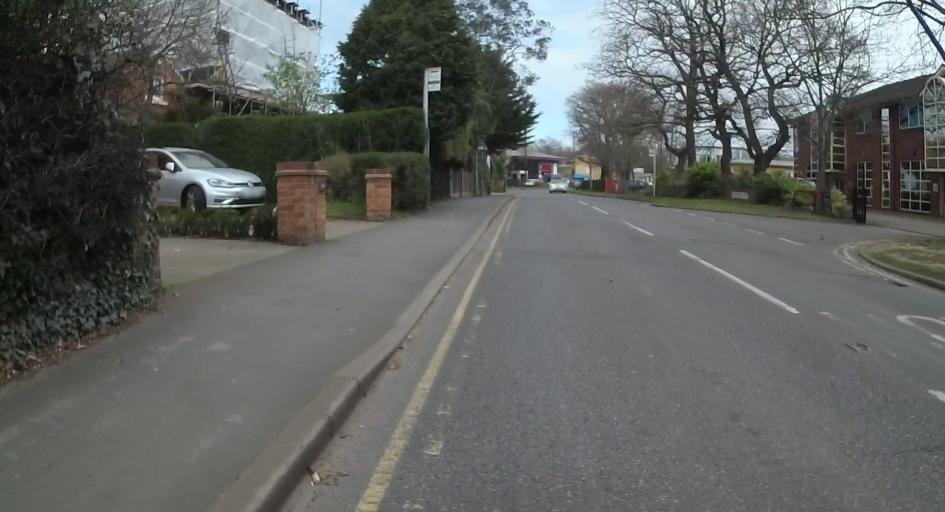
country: GB
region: England
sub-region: Surrey
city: West Byfleet
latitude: 51.3424
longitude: -0.4996
